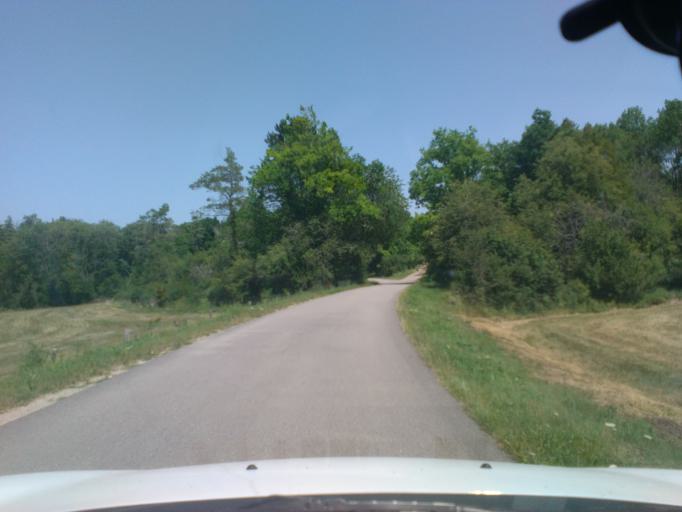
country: FR
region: Lorraine
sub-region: Departement de la Meuse
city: Gondrecourt-le-Chateau
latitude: 48.4045
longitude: 5.5107
